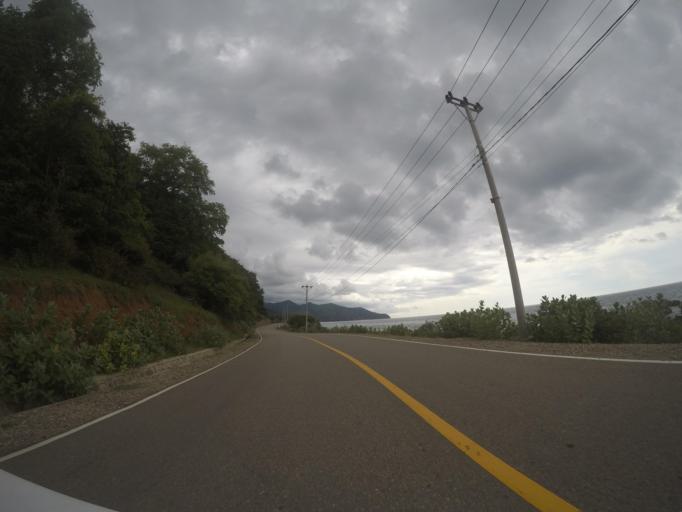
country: TL
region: Bobonaro
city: Maliana
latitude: -8.8114
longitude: 125.0839
